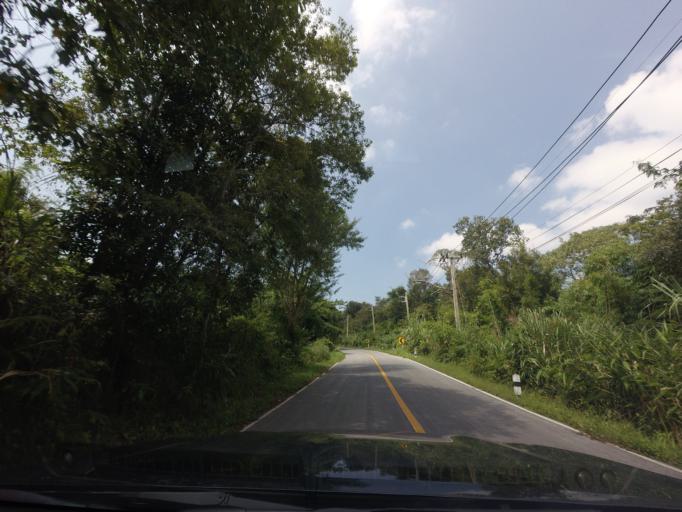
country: TH
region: Loei
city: Na Haeo
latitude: 17.4723
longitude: 100.9345
